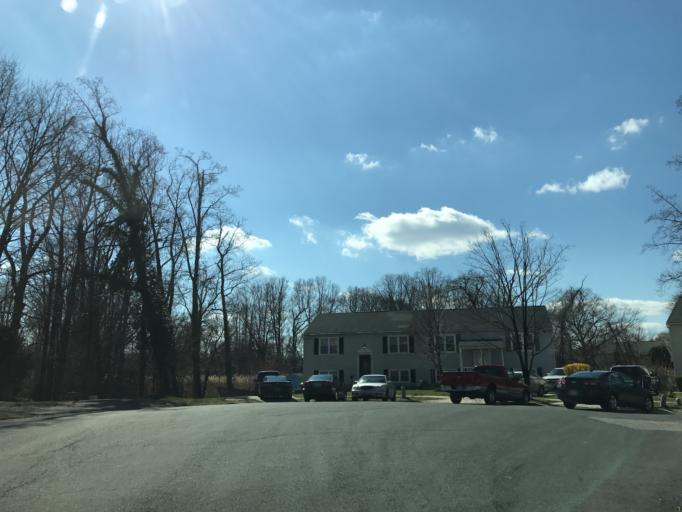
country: US
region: Maryland
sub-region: Anne Arundel County
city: Riviera Beach
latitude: 39.1652
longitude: -76.5048
